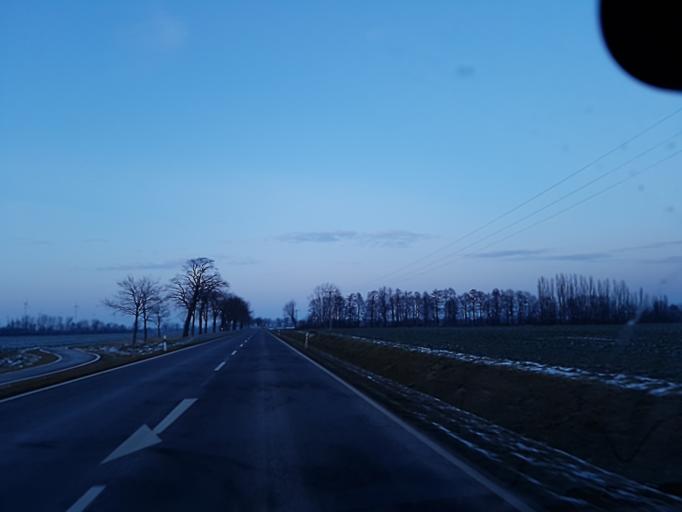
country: DE
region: Brandenburg
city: Bad Liebenwerda
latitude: 51.4929
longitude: 13.3383
